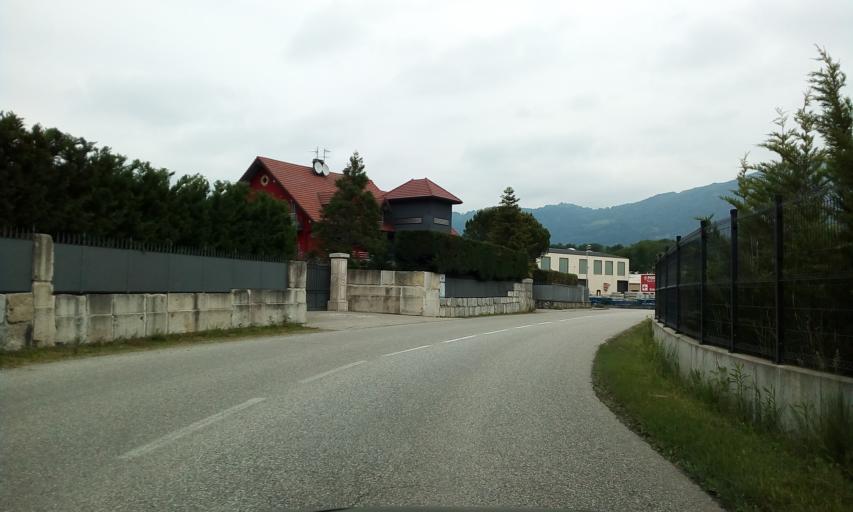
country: FR
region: Rhone-Alpes
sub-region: Departement de la Savoie
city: Saint-Baldoph
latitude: 45.5386
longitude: 5.9598
